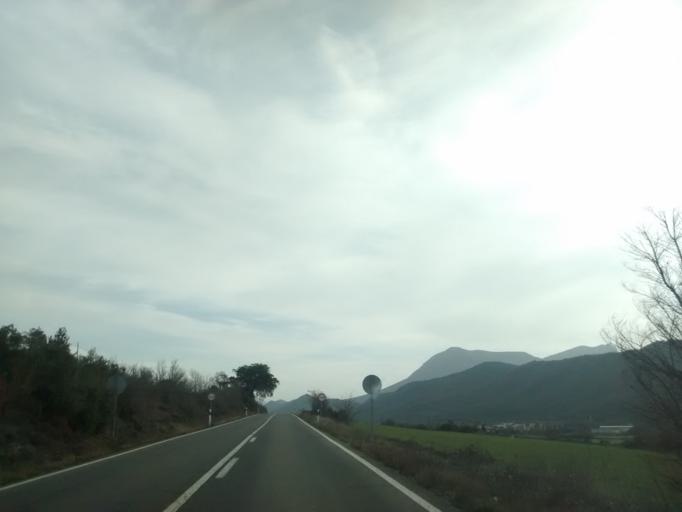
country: ES
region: Aragon
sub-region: Provincia de Huesca
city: Bailo
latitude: 42.5638
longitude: -0.7981
